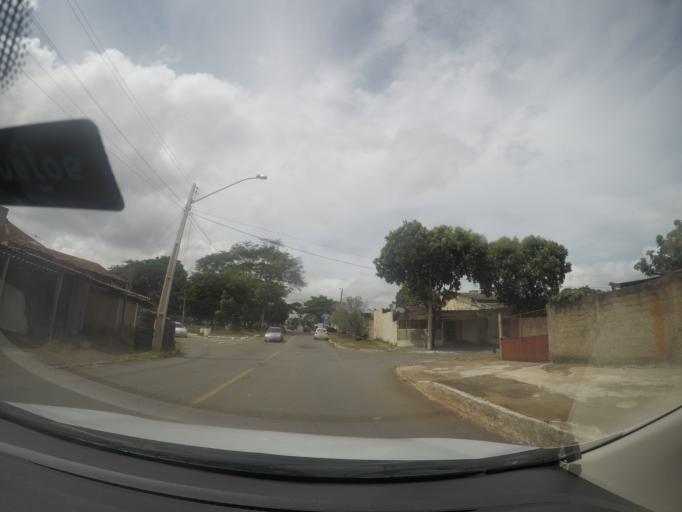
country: BR
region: Goias
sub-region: Goiania
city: Goiania
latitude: -16.7164
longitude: -49.3152
